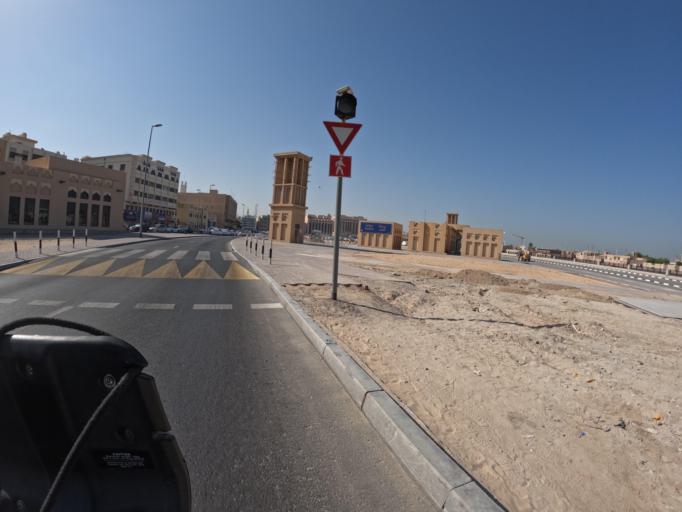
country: AE
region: Ash Shariqah
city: Sharjah
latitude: 25.2692
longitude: 55.2935
